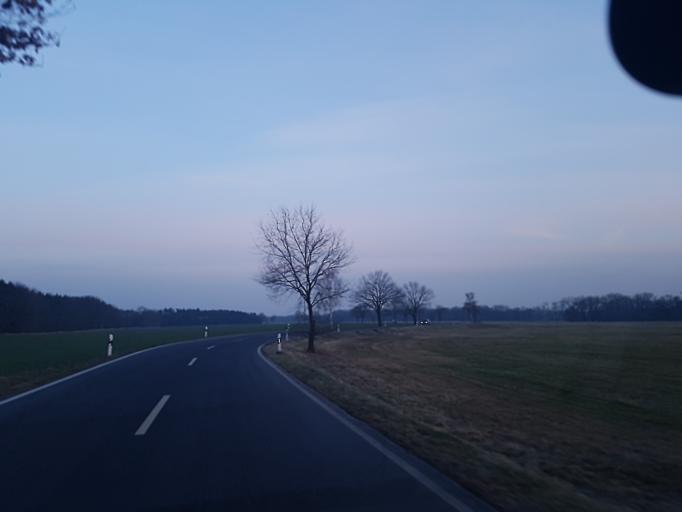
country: DE
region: Saxony-Anhalt
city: Holzdorf
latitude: 51.7553
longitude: 13.1384
